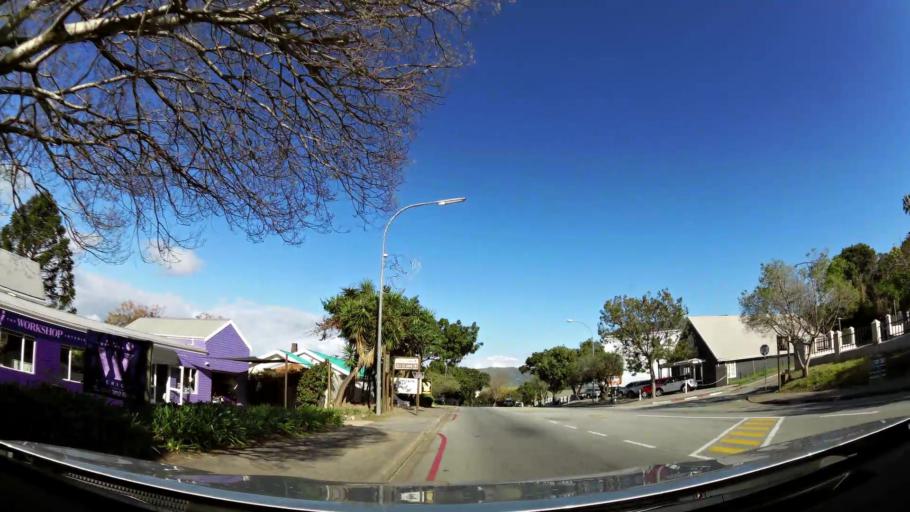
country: ZA
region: Western Cape
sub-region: Eden District Municipality
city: Knysna
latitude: -34.0357
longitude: 23.0423
